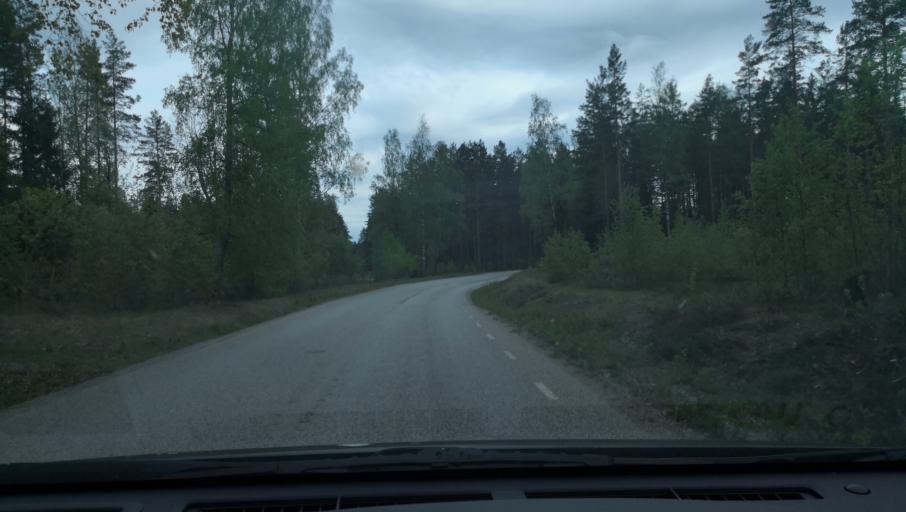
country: SE
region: Vaestmanland
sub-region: Skinnskattebergs Kommun
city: Skinnskatteberg
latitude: 59.8123
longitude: 15.5581
